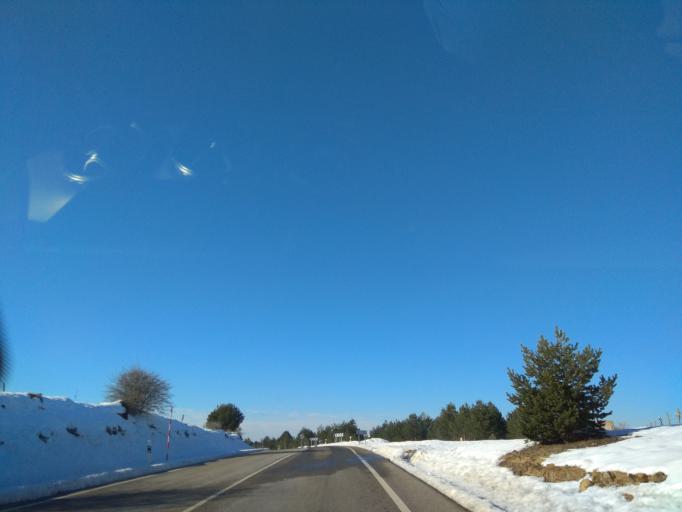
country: ES
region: Castille and Leon
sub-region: Provincia de Burgos
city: Arija
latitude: 42.9923
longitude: -3.8262
